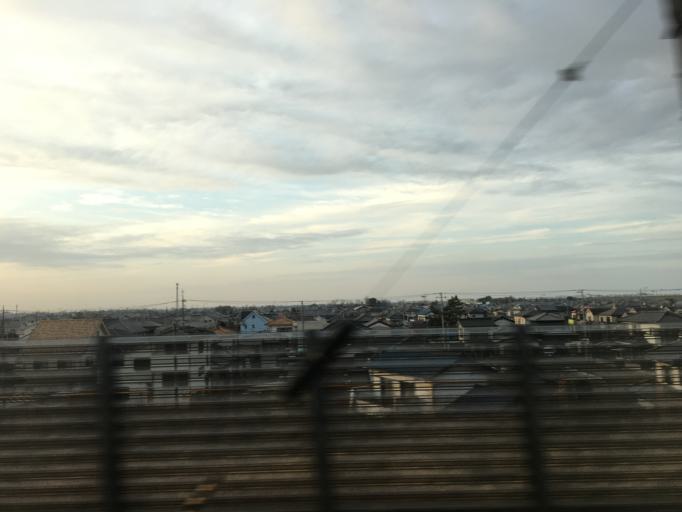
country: JP
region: Saitama
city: Kurihashi
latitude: 36.1451
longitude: 139.6964
